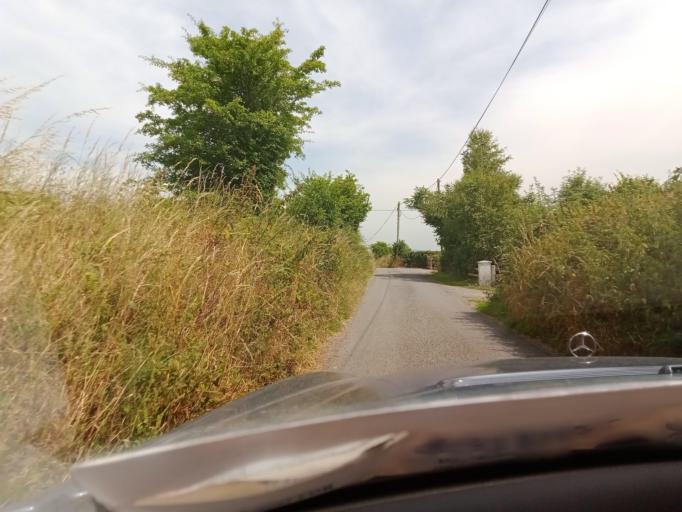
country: IE
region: Leinster
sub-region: Kilkenny
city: Mooncoin
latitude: 52.2532
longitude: -7.2105
